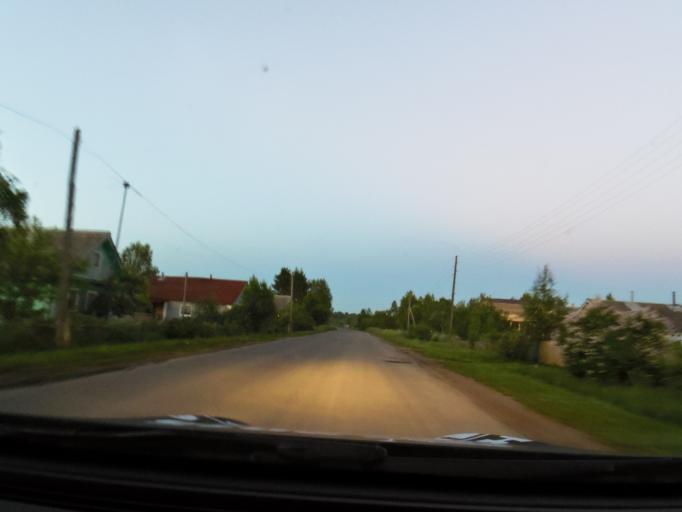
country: RU
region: Vologda
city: Vytegra
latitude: 60.9926
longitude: 36.3477
